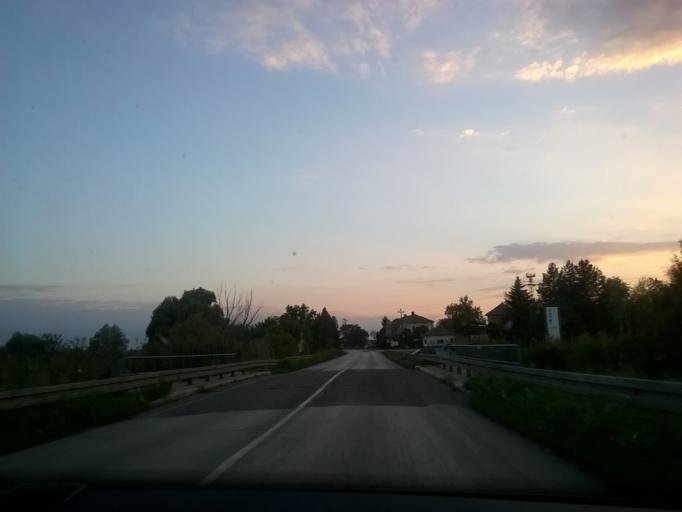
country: RS
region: Autonomna Pokrajina Vojvodina
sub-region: Juznobanatski Okrug
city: Pancevo
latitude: 44.9359
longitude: 20.6688
